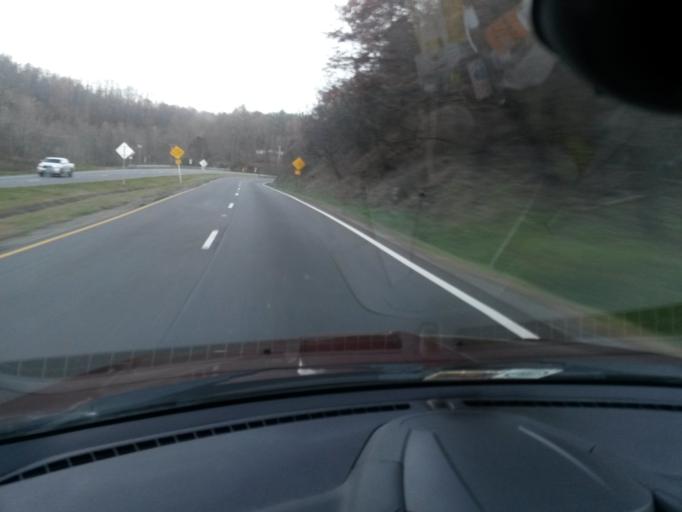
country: US
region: Virginia
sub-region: Roanoke County
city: Narrows
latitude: 37.1526
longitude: -79.9572
